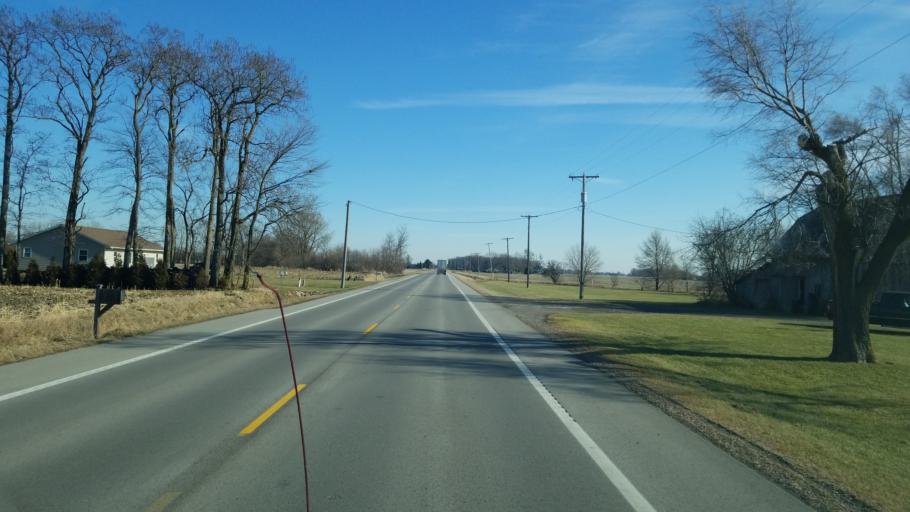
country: US
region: Ohio
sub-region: Henry County
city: Liberty Center
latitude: 41.3712
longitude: -83.9783
